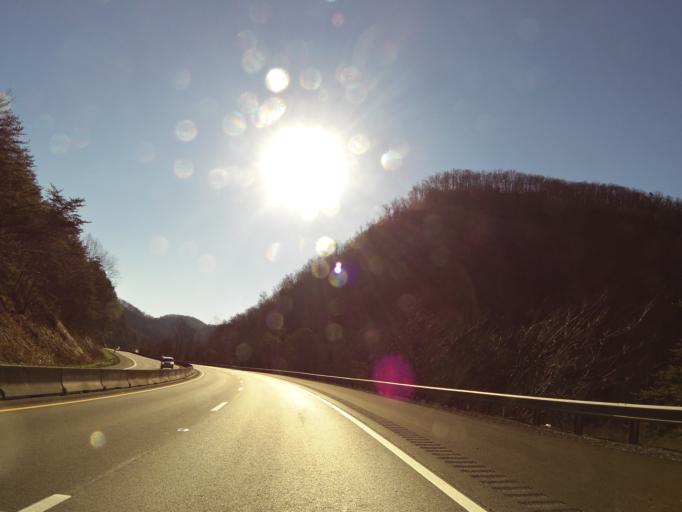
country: US
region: Tennessee
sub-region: Cocke County
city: Newport
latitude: 35.8104
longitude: -83.1427
